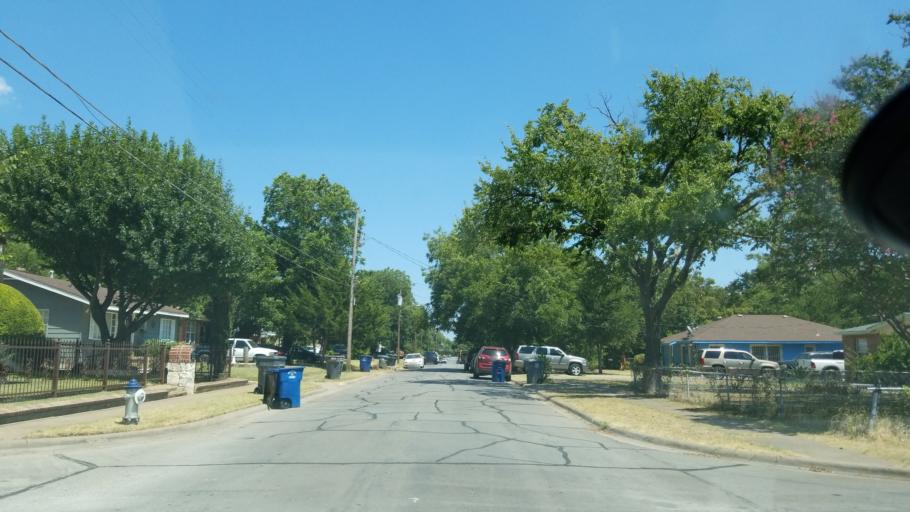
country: US
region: Texas
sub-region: Dallas County
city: Cockrell Hill
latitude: 32.7244
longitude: -96.8884
